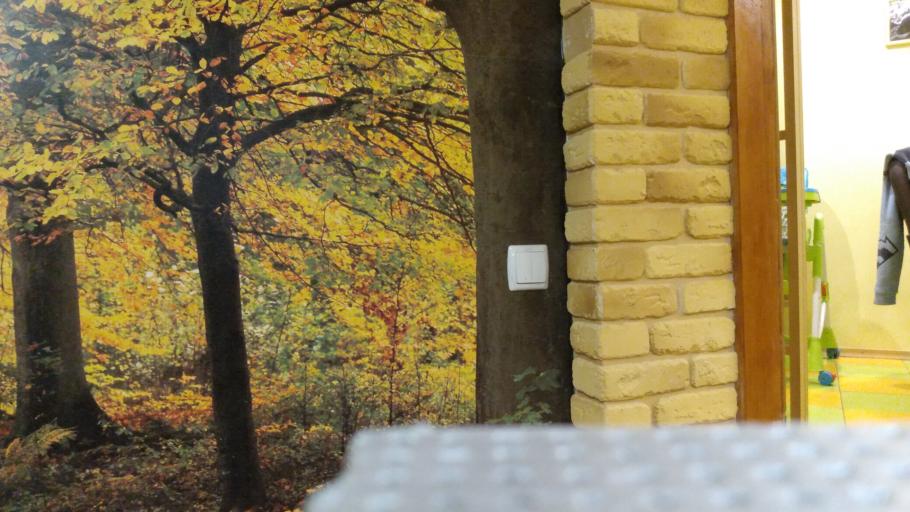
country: RU
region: Vologda
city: Babayevo
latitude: 59.3673
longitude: 35.9974
